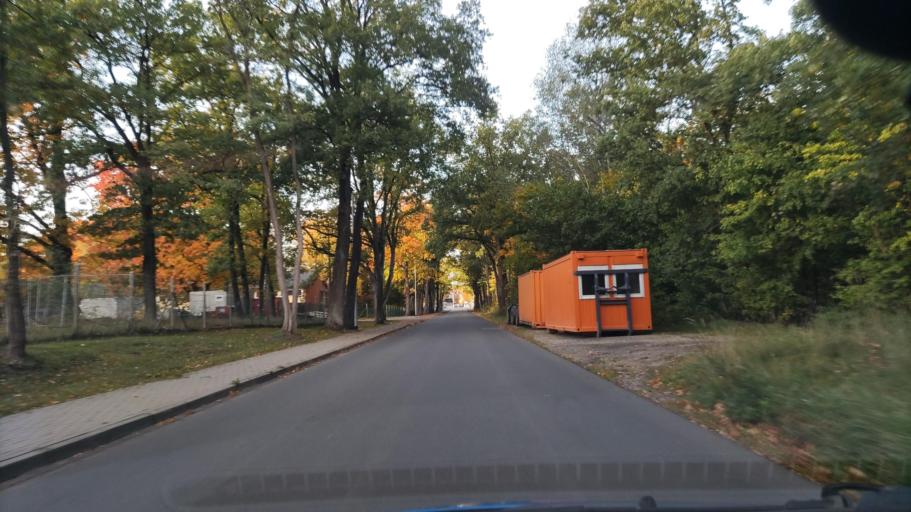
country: DE
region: Lower Saxony
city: Munster
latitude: 52.9827
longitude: 10.0755
